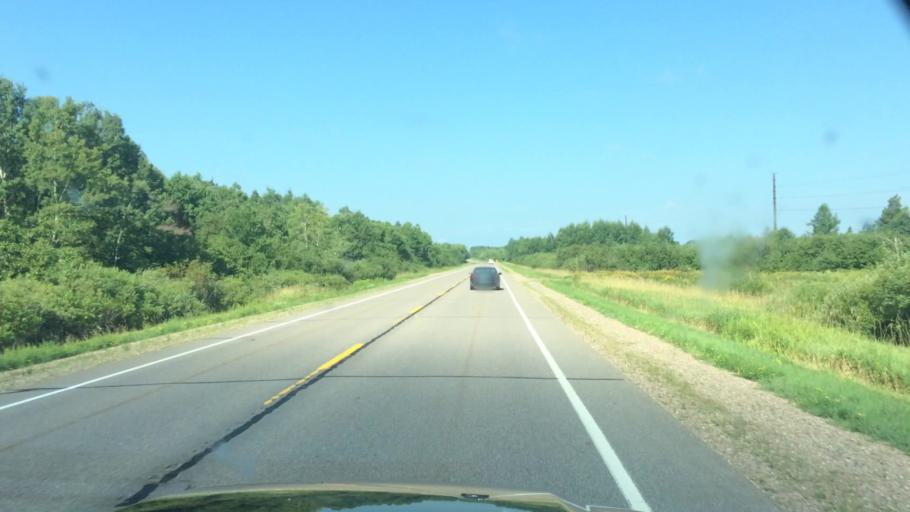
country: US
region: Wisconsin
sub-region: Langlade County
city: Antigo
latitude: 45.1465
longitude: -89.3365
